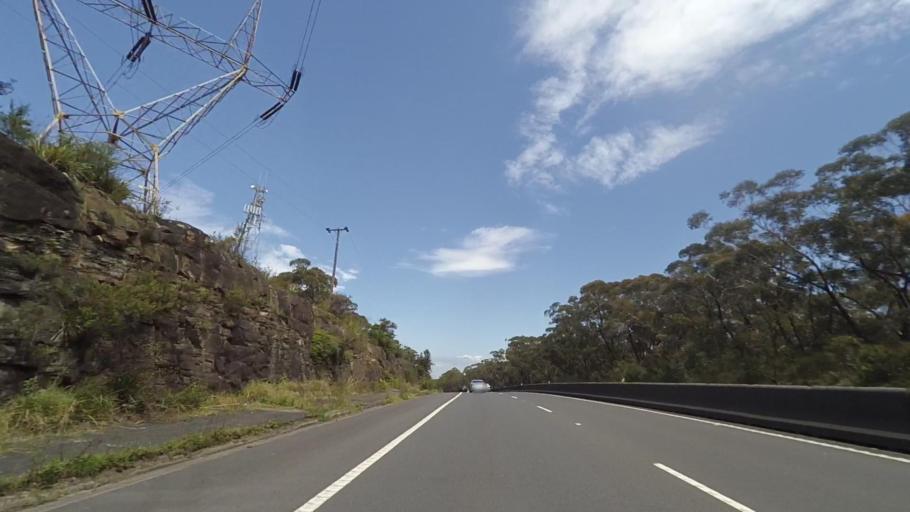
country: AU
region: New South Wales
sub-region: Wollongong
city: Bulli
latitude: -34.3227
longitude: 150.8819
